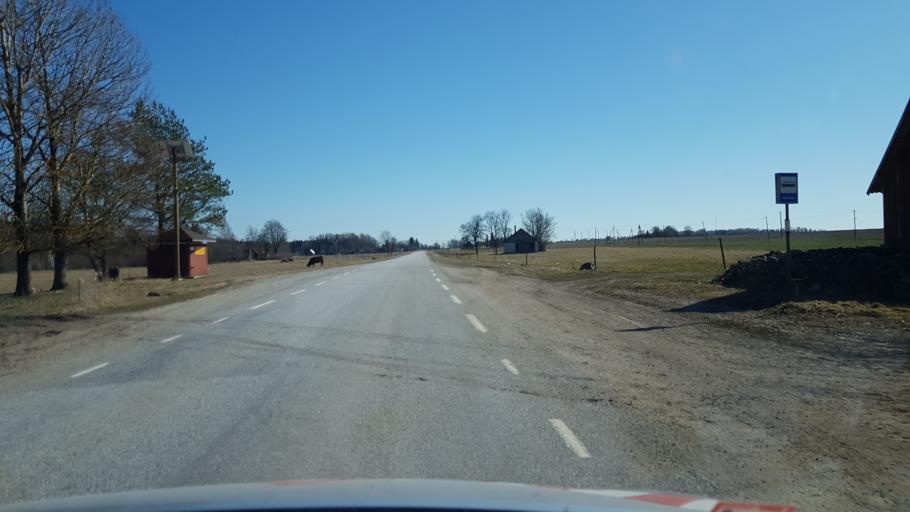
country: EE
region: Jaervamaa
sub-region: Koeru vald
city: Koeru
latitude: 59.0505
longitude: 26.0883
